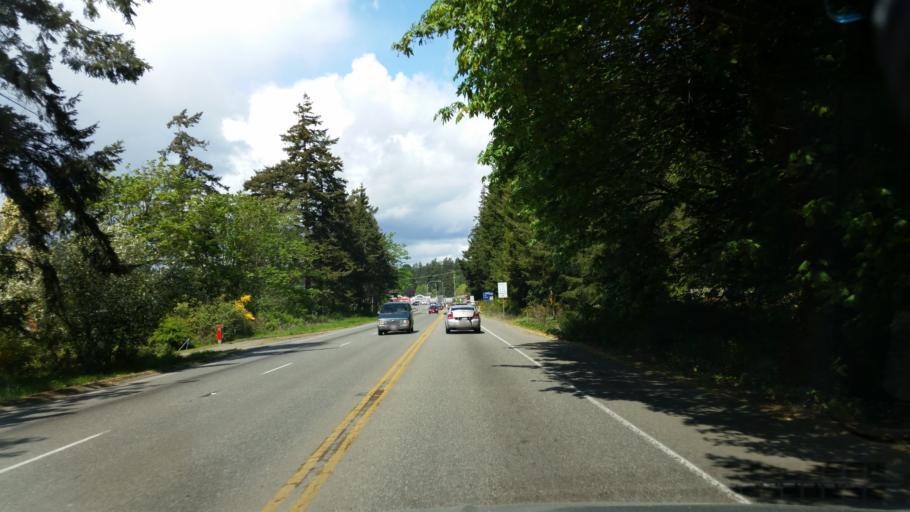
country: US
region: Washington
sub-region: Pierce County
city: Purdy
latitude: 47.3806
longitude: -122.6247
